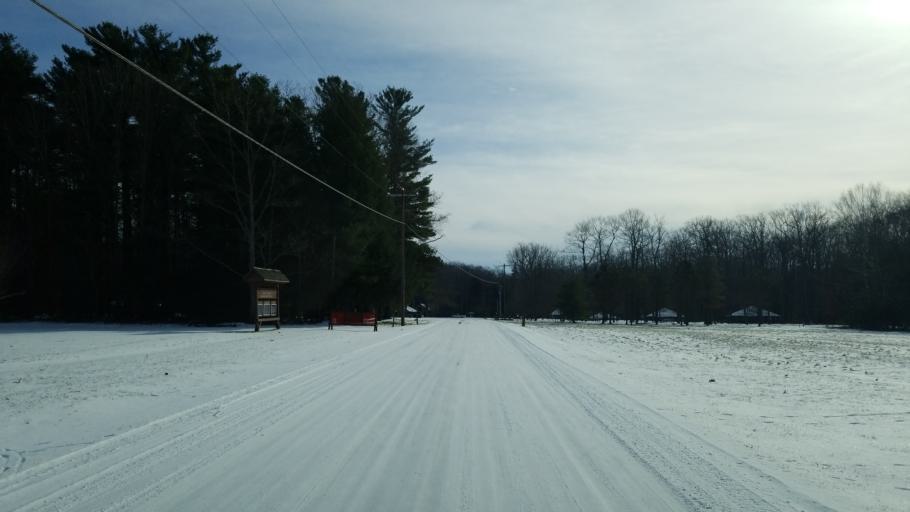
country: US
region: Pennsylvania
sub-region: Clearfield County
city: Clearfield
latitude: 41.1151
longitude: -78.5275
